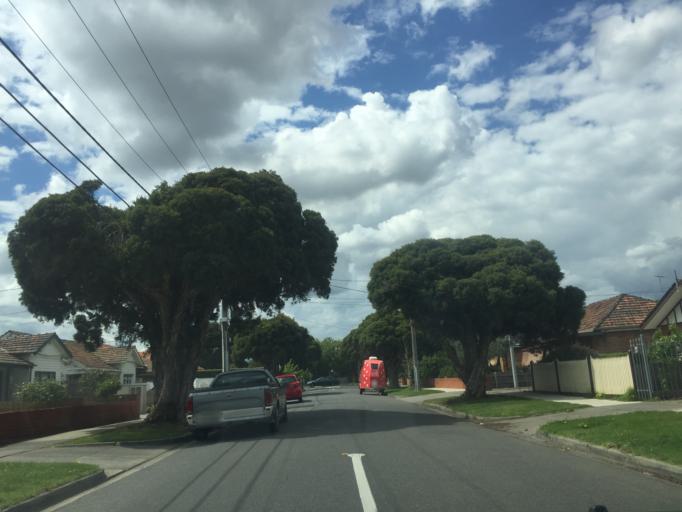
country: AU
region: Victoria
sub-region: Darebin
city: Reservoir
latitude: -37.7158
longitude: 145.0132
